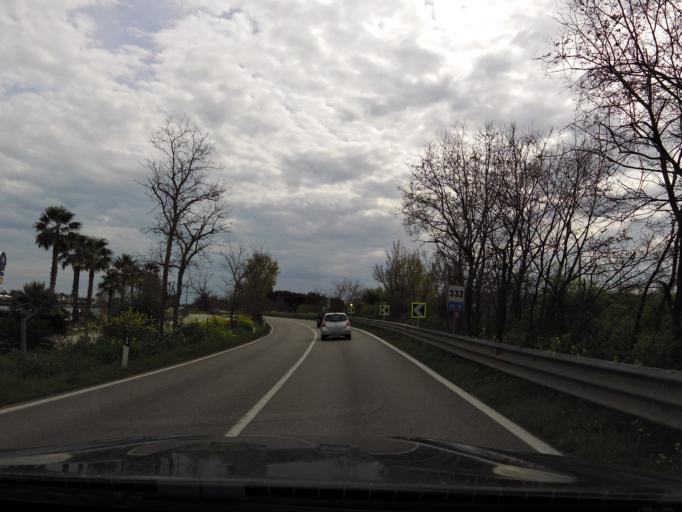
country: IT
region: The Marches
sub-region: Provincia di Macerata
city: Porto Potenza Picena
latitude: 43.3947
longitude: 13.6796
